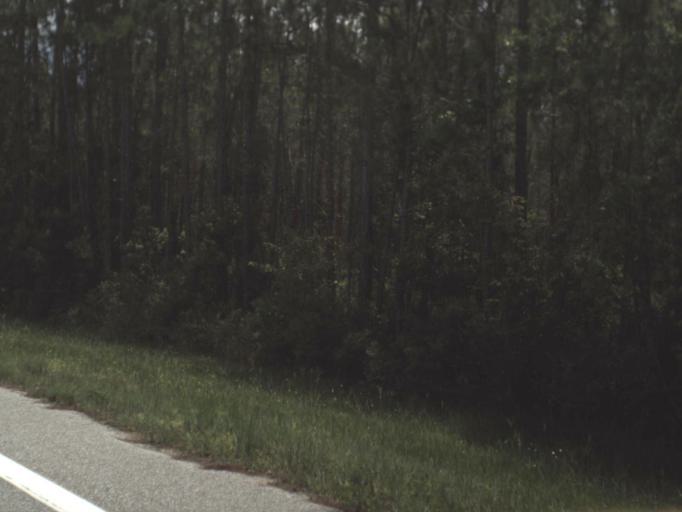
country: US
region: Florida
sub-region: Levy County
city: Bronson
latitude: 29.3370
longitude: -82.7515
